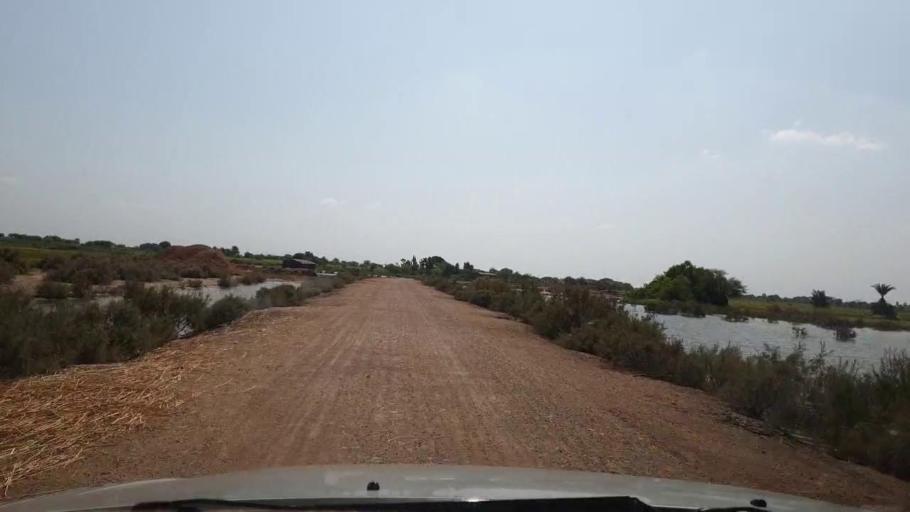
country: PK
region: Sindh
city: Rajo Khanani
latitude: 25.0001
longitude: 68.7712
